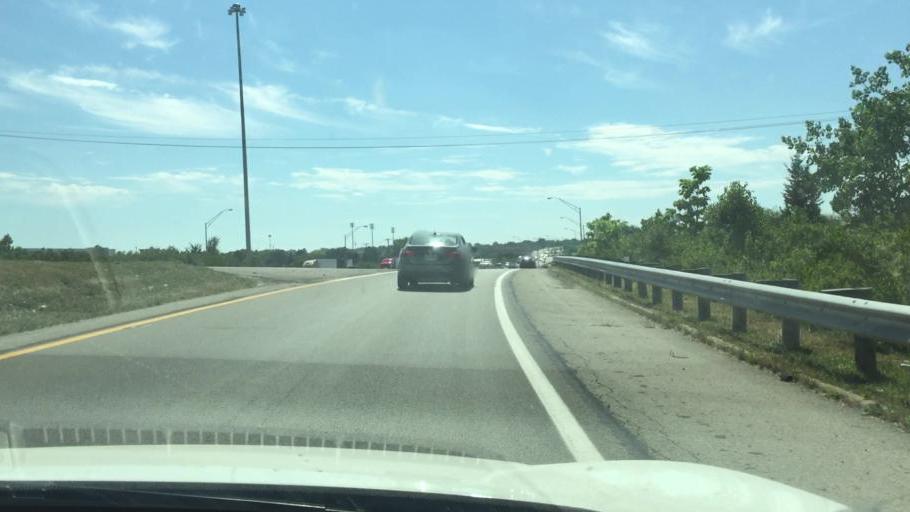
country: US
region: Ohio
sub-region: Franklin County
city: Columbus
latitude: 39.9512
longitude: -83.0194
